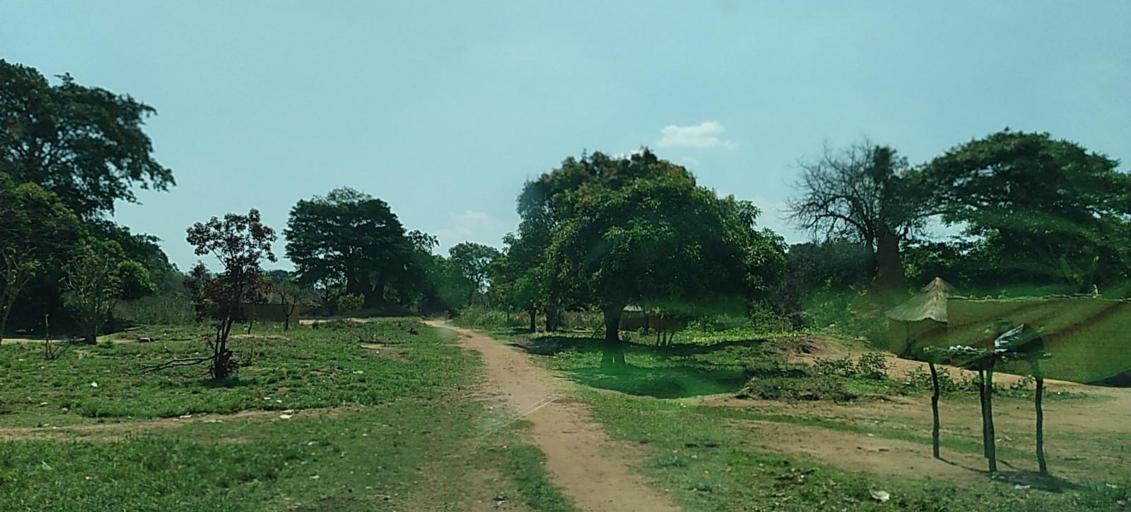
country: CD
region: Katanga
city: Kolwezi
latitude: -11.2789
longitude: 25.1258
